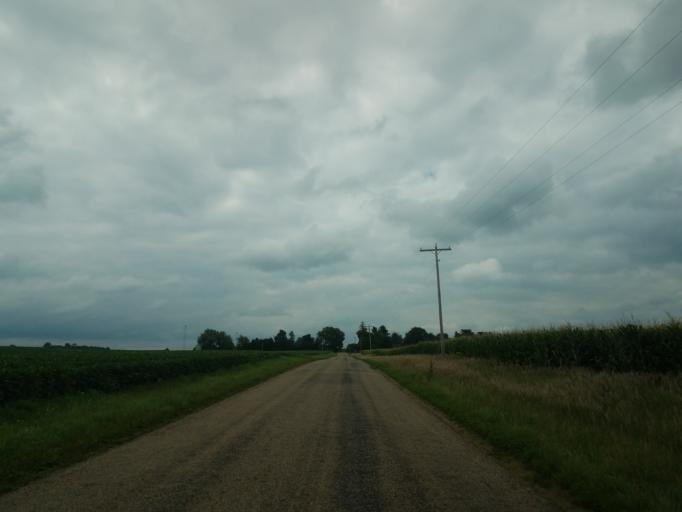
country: US
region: Illinois
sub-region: McLean County
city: Twin Grove
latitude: 40.4187
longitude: -89.0621
